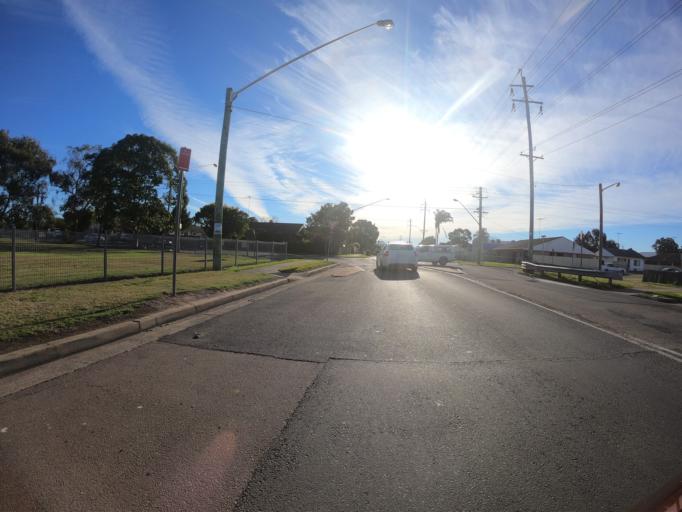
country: AU
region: New South Wales
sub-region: Hawkesbury
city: South Windsor
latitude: -33.6236
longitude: 150.8046
